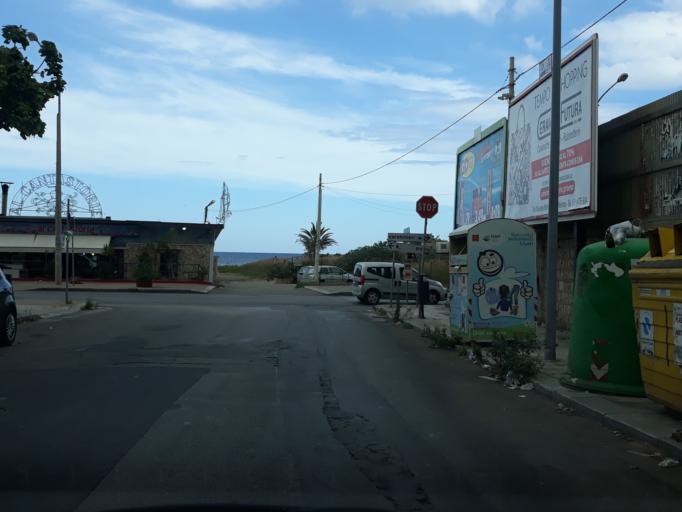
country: IT
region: Sicily
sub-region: Palermo
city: Ciaculli
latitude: 38.1025
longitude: 13.3947
